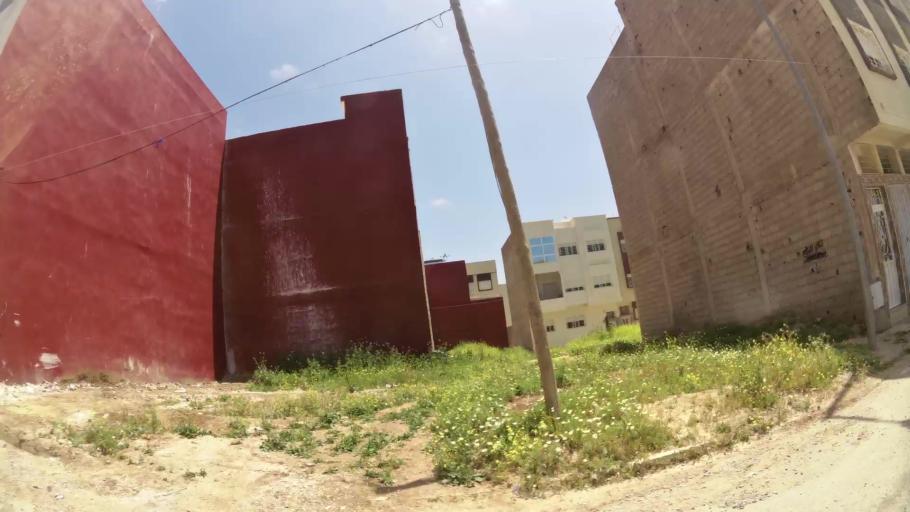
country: MA
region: Fes-Boulemane
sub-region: Fes
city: Fes
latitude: 34.0510
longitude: -5.0441
